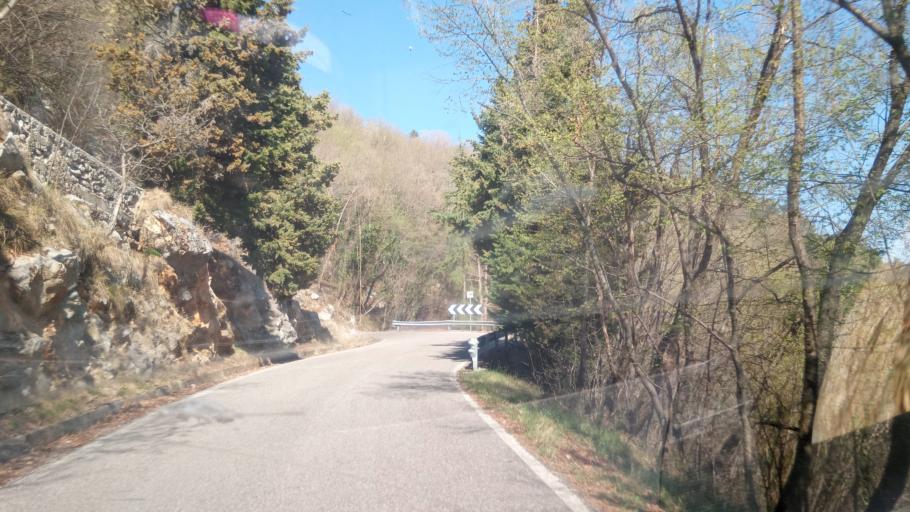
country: IT
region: Veneto
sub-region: Provincia di Treviso
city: Borso del Grappa
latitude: 45.8171
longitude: 11.7639
